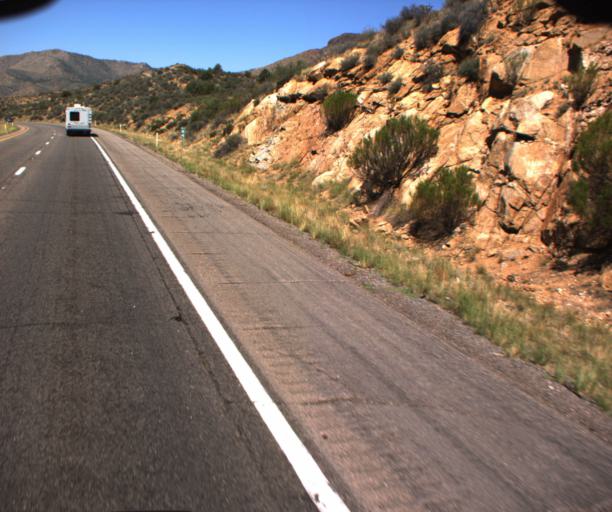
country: US
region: Arizona
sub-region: Mohave County
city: Peach Springs
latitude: 35.1791
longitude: -113.4915
